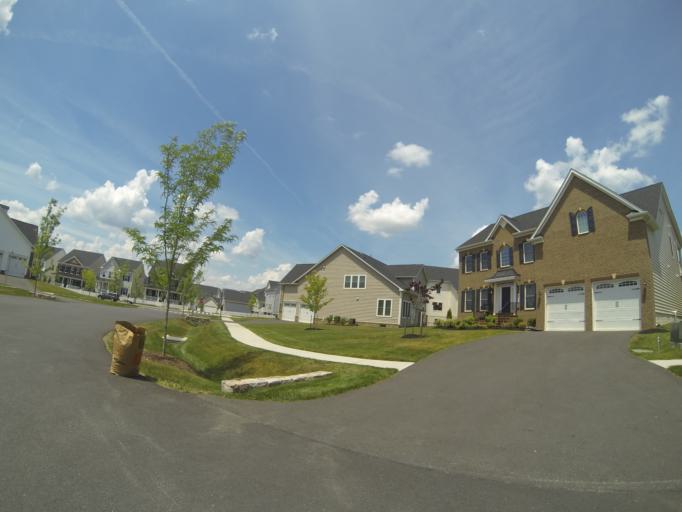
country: US
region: Maryland
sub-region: Montgomery County
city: Clarksburg
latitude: 39.2238
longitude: -77.2394
